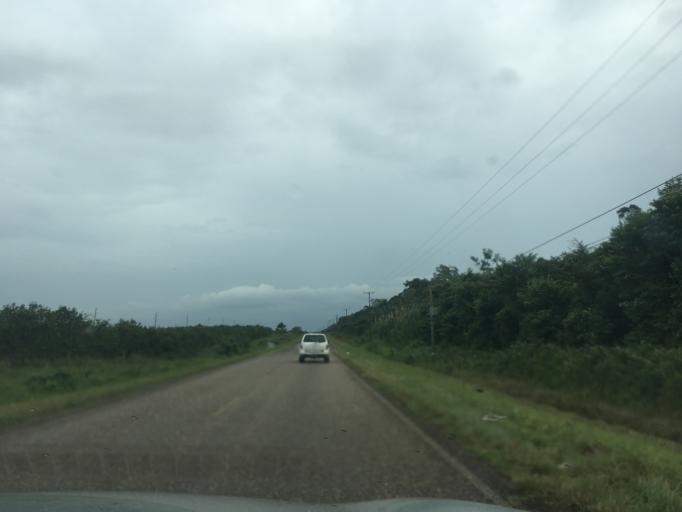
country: BZ
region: Stann Creek
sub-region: Dangriga
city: Dangriga
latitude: 16.9458
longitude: -88.3275
